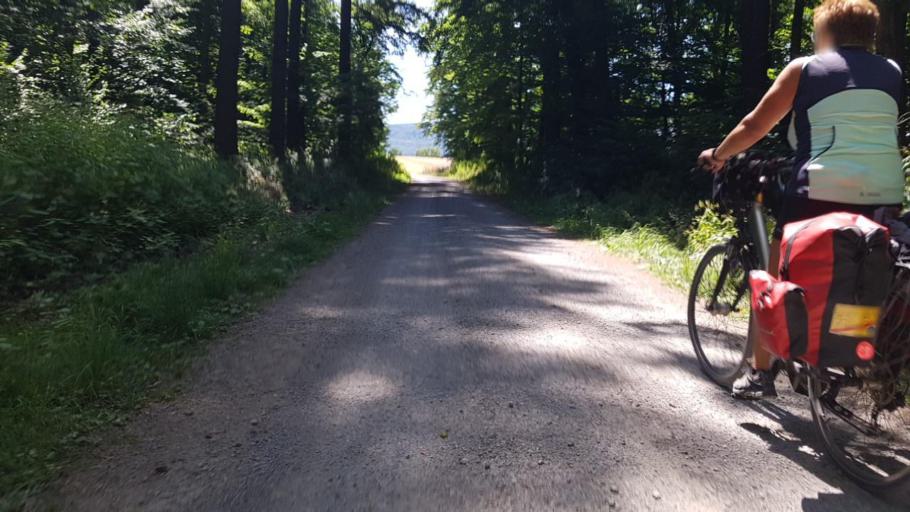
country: DE
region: Baden-Wuerttemberg
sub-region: Regierungsbezirk Stuttgart
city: Zaberfeld
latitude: 49.0694
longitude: 8.9207
